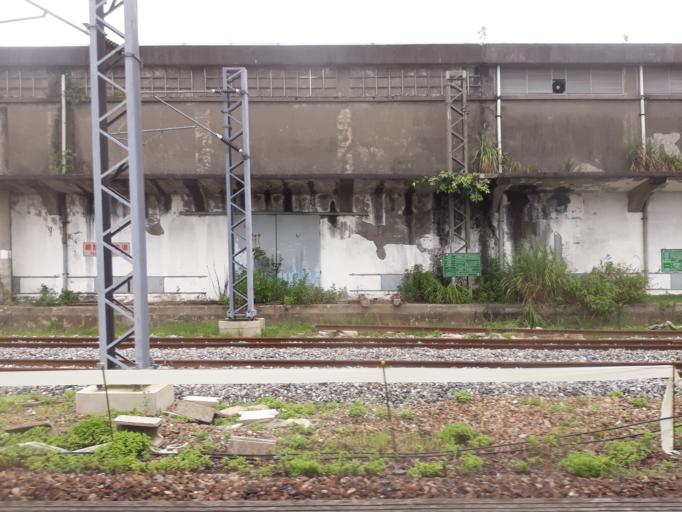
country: TW
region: Taiwan
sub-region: Yilan
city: Yilan
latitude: 24.6946
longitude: 121.7752
